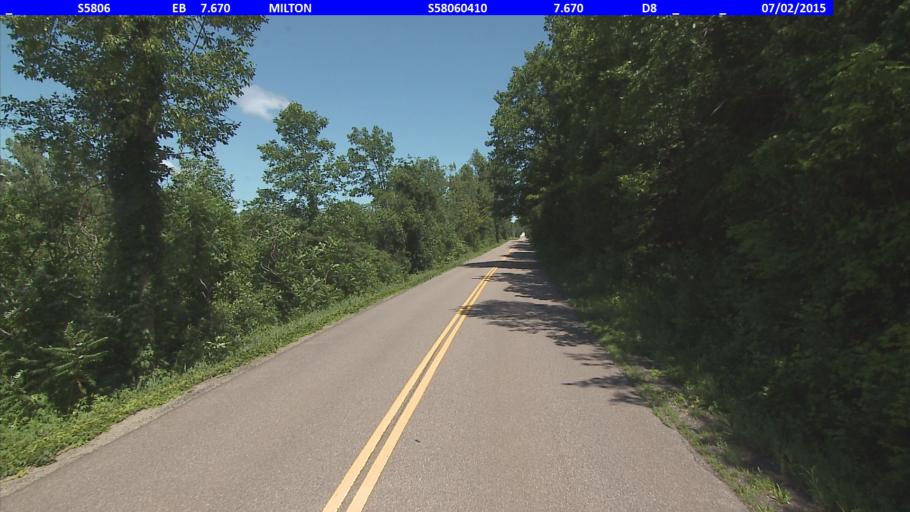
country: US
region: Vermont
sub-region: Chittenden County
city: Milton
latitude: 44.7065
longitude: -73.2063
